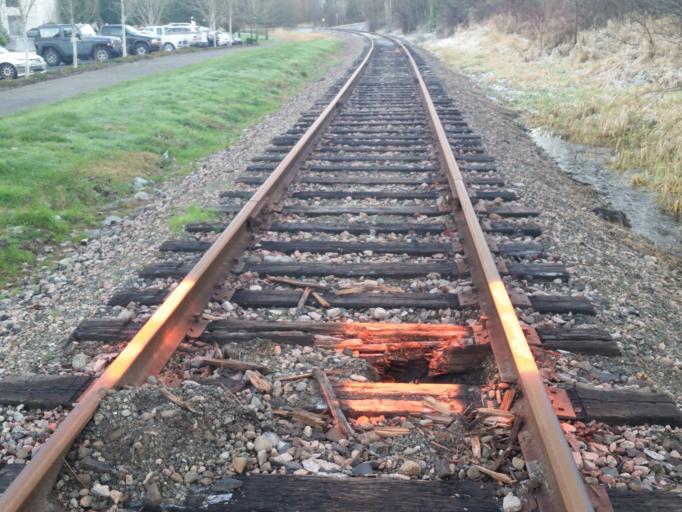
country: US
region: Washington
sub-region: King County
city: Woodinville
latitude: 47.7380
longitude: -122.1556
